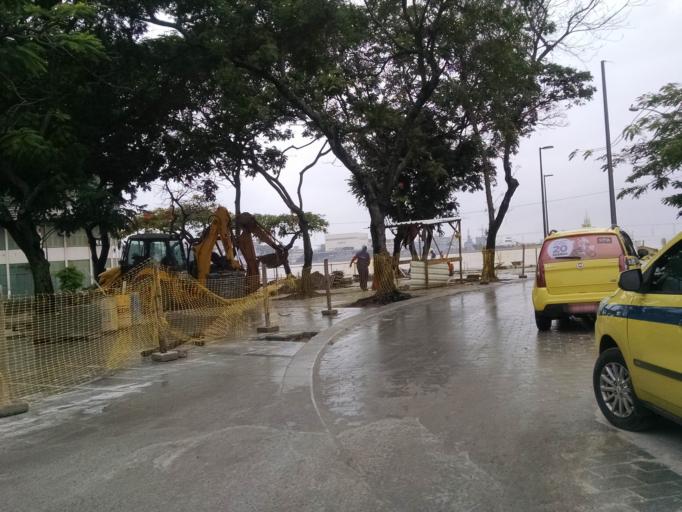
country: BR
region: Rio de Janeiro
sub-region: Rio De Janeiro
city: Rio de Janeiro
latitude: -22.9049
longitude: -43.1699
